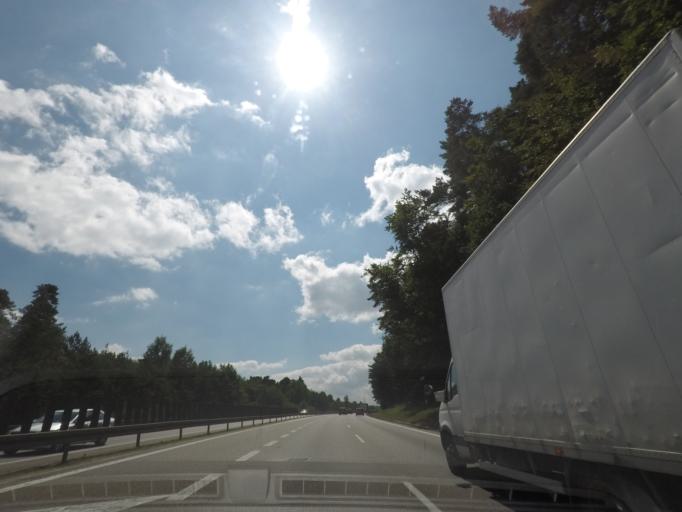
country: PL
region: Pomeranian Voivodeship
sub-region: Gdynia
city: Wielki Kack
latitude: 54.4816
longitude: 18.4729
